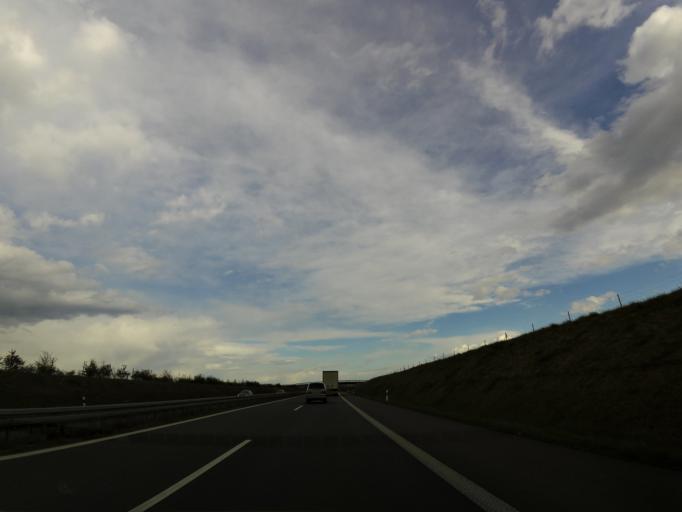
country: DE
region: Saxony-Anhalt
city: Quedlinburg
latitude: 51.8138
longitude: 11.1674
